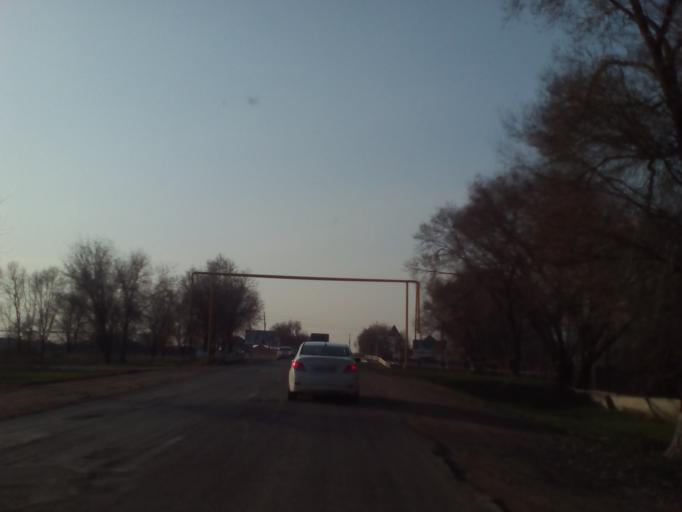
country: KZ
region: Almaty Oblysy
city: Burunday
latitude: 43.1736
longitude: 76.5279
